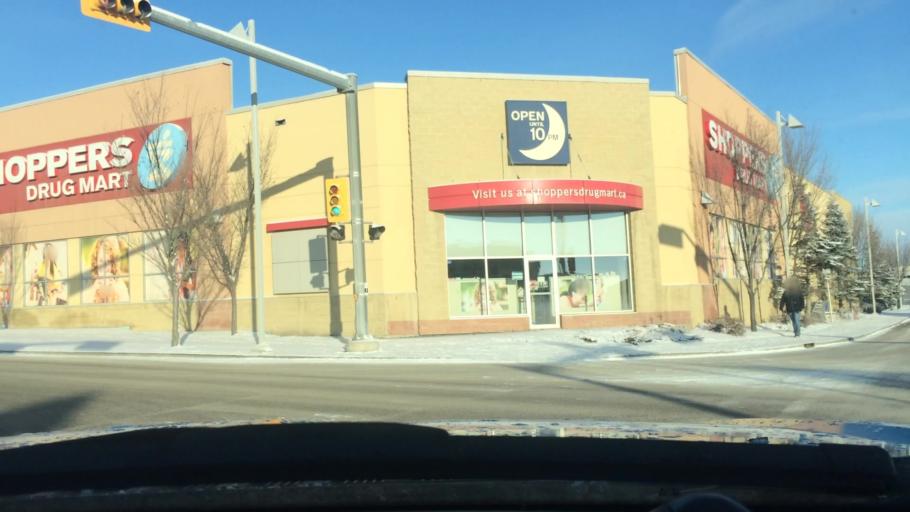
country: CA
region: Alberta
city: Calgary
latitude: 51.1573
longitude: -114.1600
